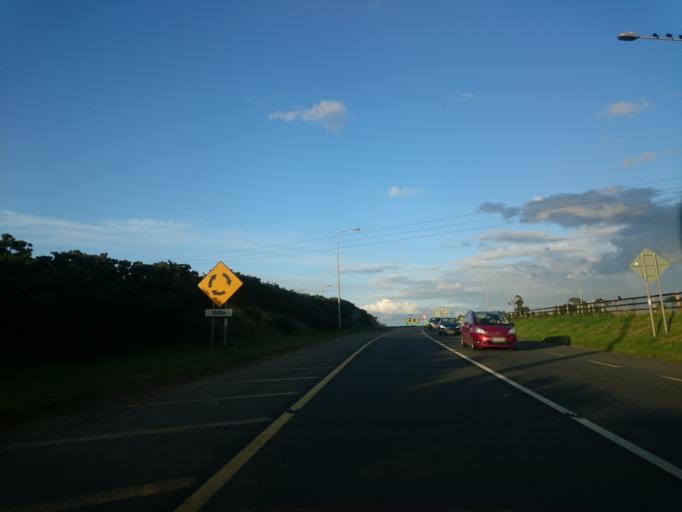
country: IE
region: Leinster
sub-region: Loch Garman
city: Gorey
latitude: 52.6329
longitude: -6.3753
